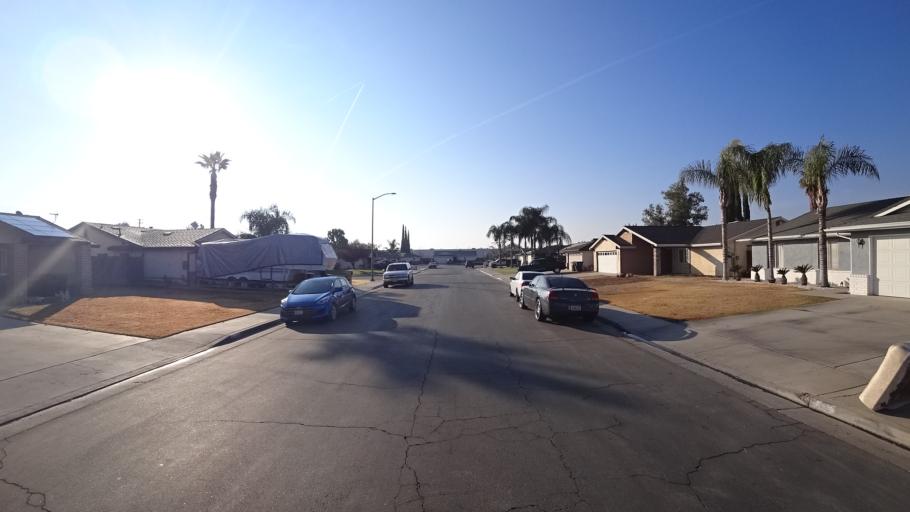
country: US
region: California
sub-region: Kern County
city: Greenfield
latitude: 35.3009
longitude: -119.0265
